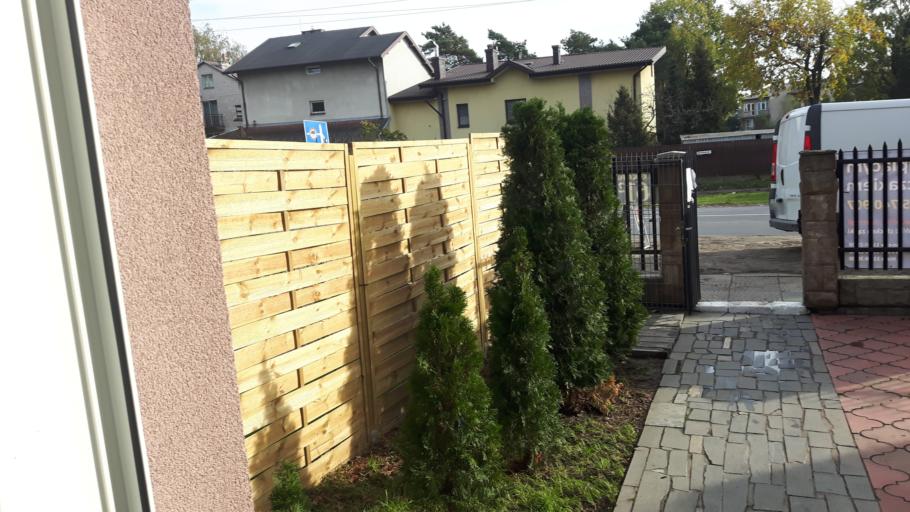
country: PL
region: Masovian Voivodeship
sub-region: Powiat wolominski
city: Zabki
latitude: 52.2907
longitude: 21.1240
